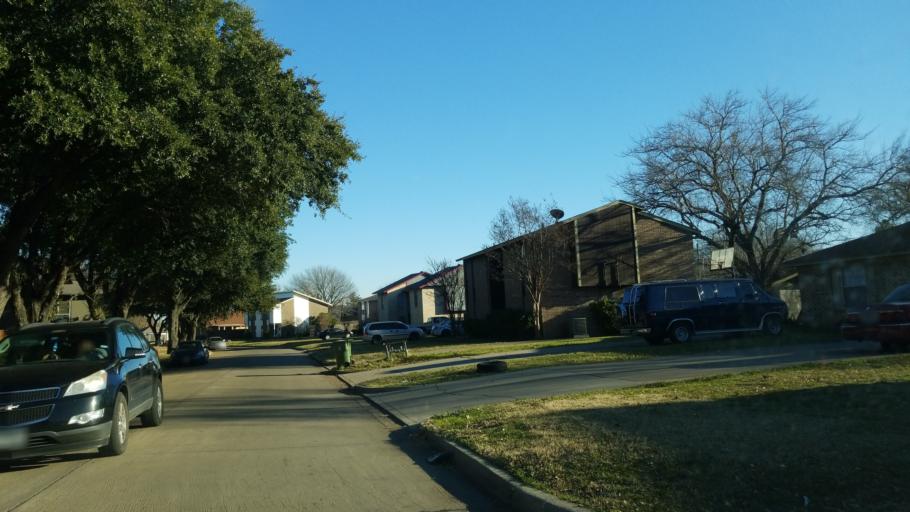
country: US
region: Texas
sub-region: Tarrant County
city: Arlington
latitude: 32.7330
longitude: -97.0680
